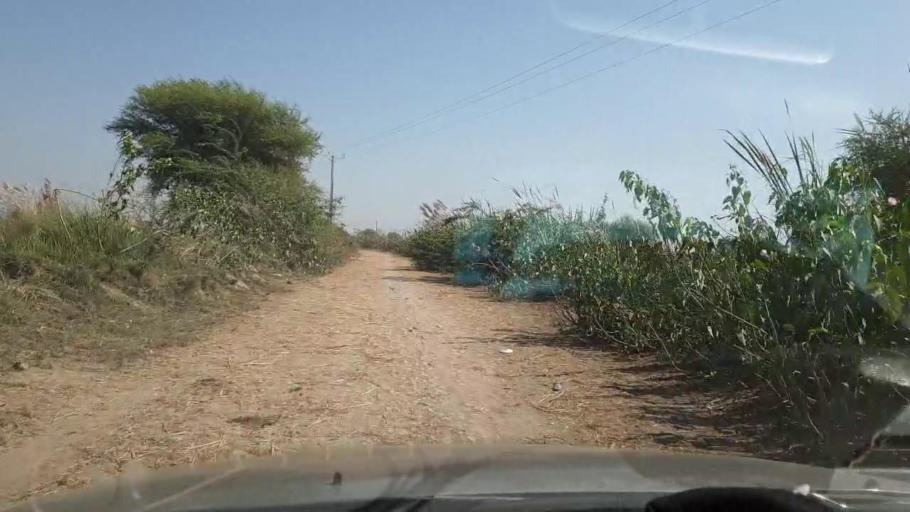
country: PK
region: Sindh
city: Daro Mehar
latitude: 24.9692
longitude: 68.1184
